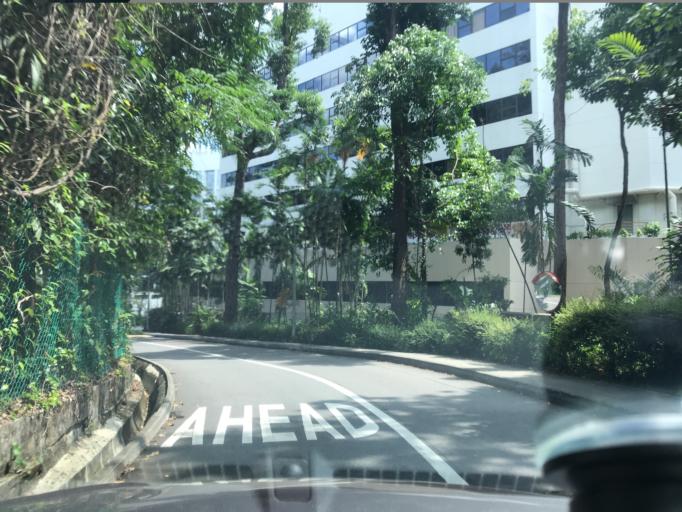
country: SG
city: Singapore
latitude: 1.3084
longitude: 103.8204
